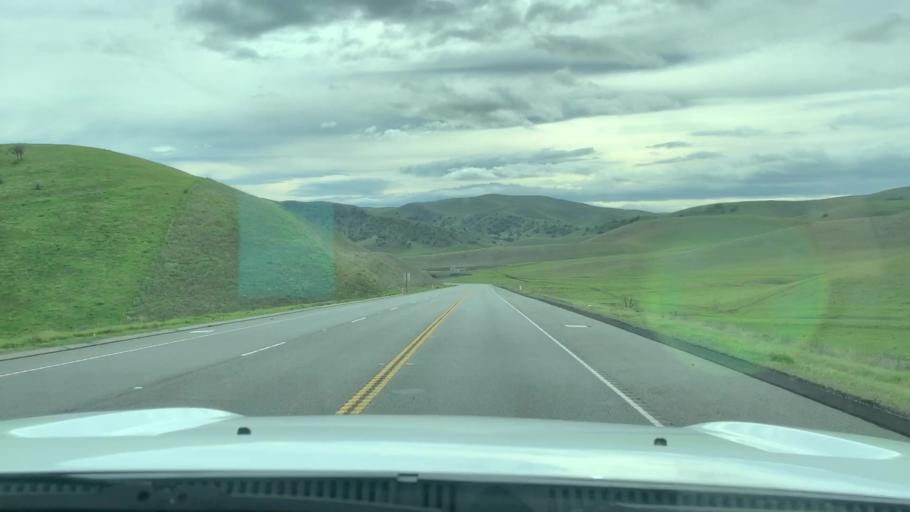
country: US
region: California
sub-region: San Luis Obispo County
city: Shandon
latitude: 35.7392
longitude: -120.2098
